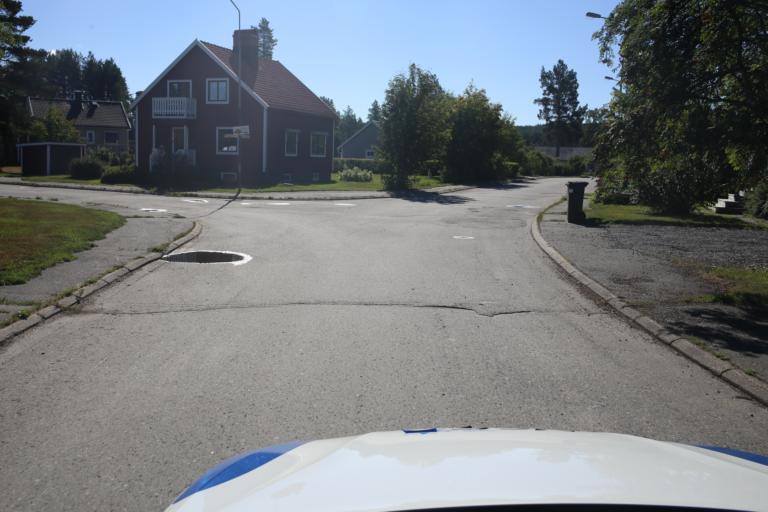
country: SE
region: Vaesterbotten
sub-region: Skelleftea Kommun
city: Viken
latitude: 64.7467
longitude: 20.7667
